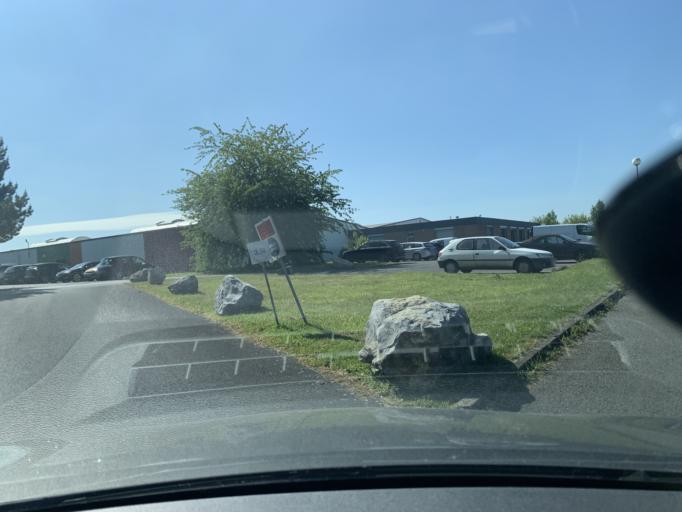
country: FR
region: Nord-Pas-de-Calais
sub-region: Departement du Nord
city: Rumilly-en-Cambresis
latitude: 50.1461
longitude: 3.2241
